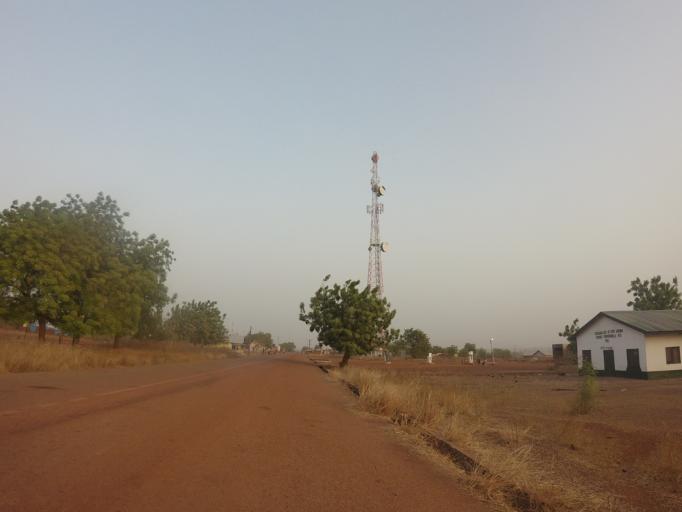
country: GH
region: Northern
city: Tamale
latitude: 9.4456
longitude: -1.1180
